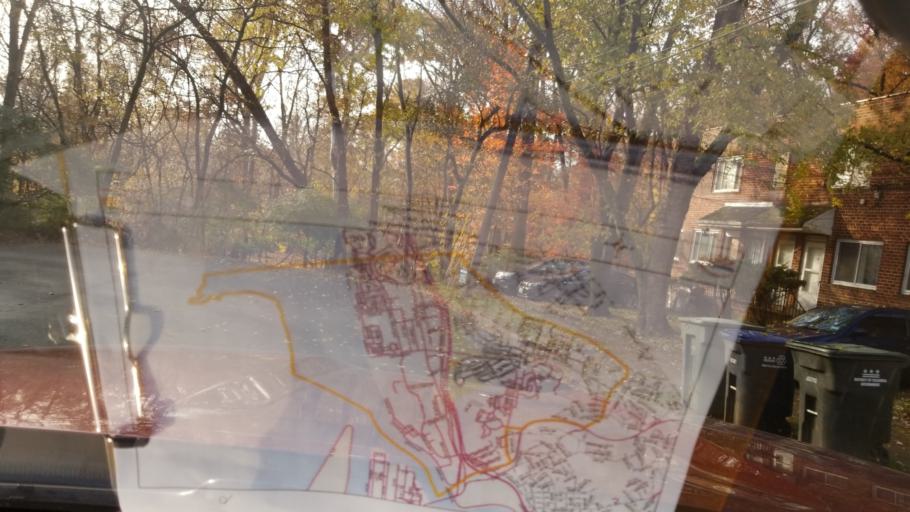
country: US
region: Maryland
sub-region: Prince George's County
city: Glassmanor
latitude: 38.8202
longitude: -77.0054
